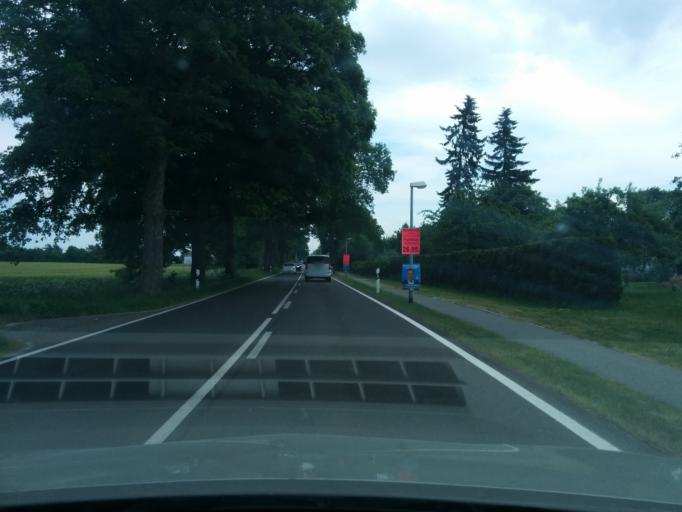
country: DE
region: Mecklenburg-Vorpommern
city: Jarmen
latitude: 53.9437
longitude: 13.3905
